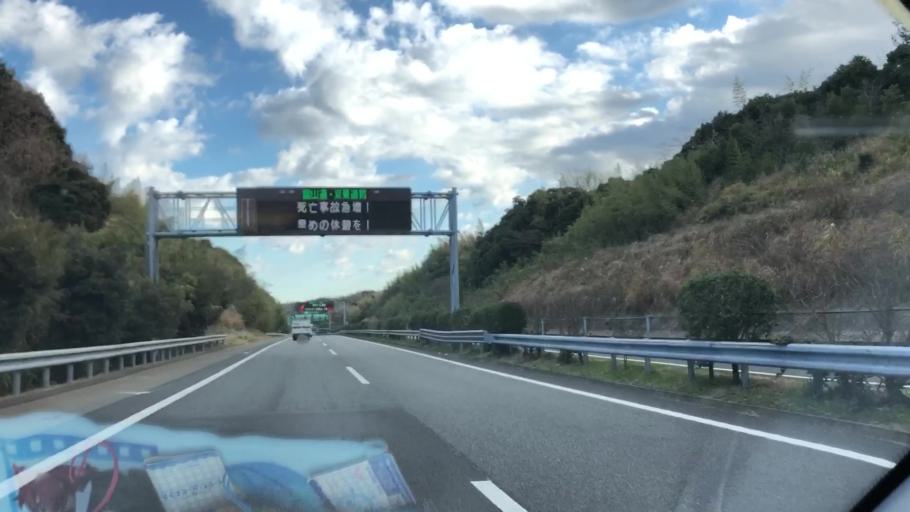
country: JP
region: Chiba
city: Kisarazu
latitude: 35.3685
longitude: 139.9667
